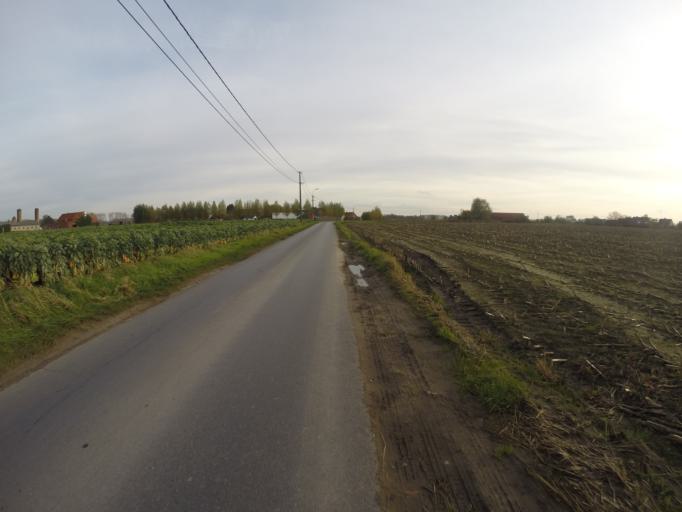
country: BE
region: Flanders
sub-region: Provincie Oost-Vlaanderen
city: Aalter
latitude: 51.0593
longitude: 3.4783
